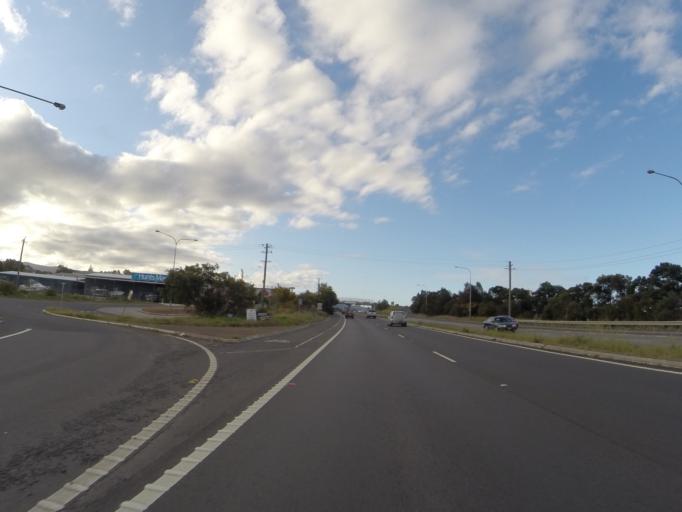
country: AU
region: New South Wales
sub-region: Shellharbour
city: Albion Park Rail
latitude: -34.5440
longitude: 150.7850
